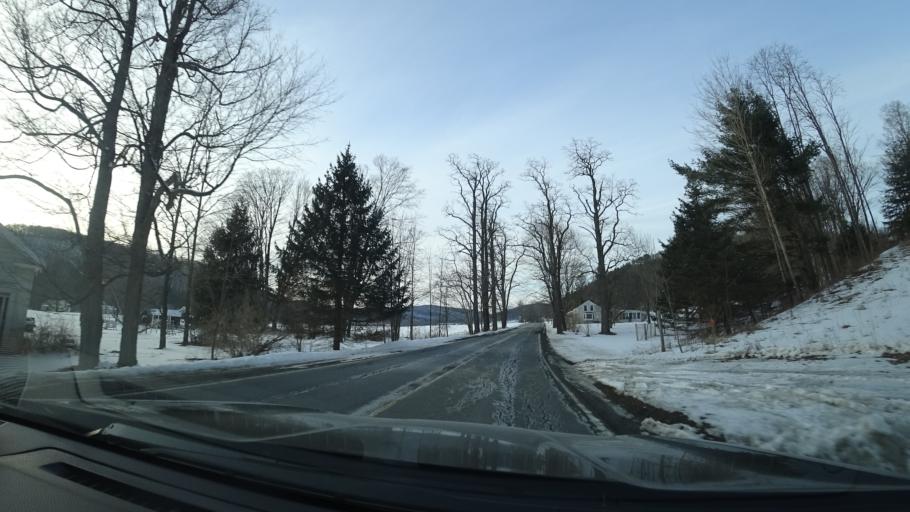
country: US
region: New York
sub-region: Washington County
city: Cambridge
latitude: 43.1773
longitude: -73.3643
